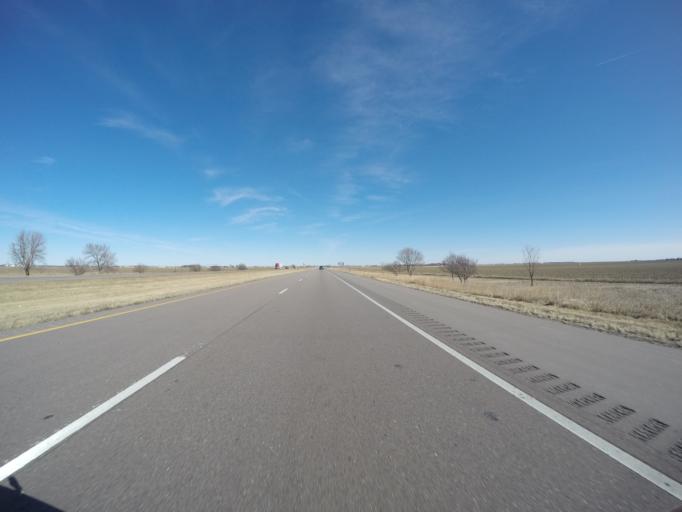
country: US
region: Nebraska
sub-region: York County
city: York
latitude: 40.8211
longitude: -97.6351
